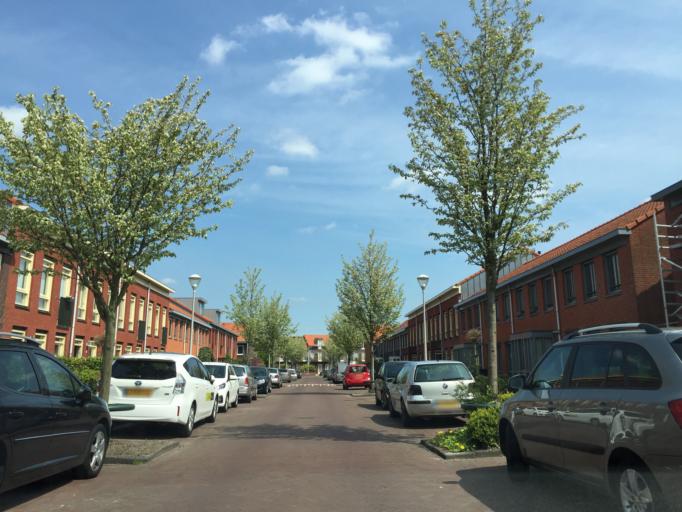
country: NL
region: South Holland
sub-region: Gemeente Den Haag
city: Ypenburg
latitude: 52.0438
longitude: 4.3741
